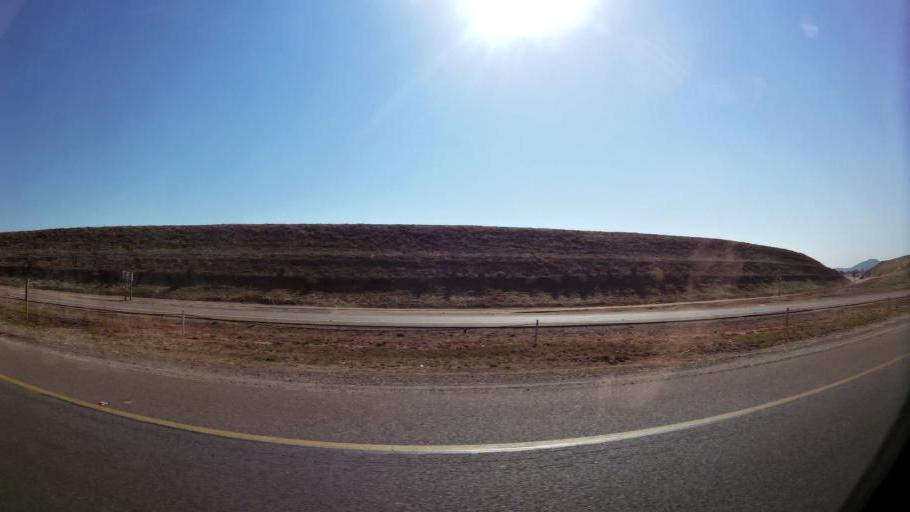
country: ZA
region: Gauteng
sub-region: City of Tshwane Metropolitan Municipality
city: Pretoria
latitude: -25.6549
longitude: 28.1093
